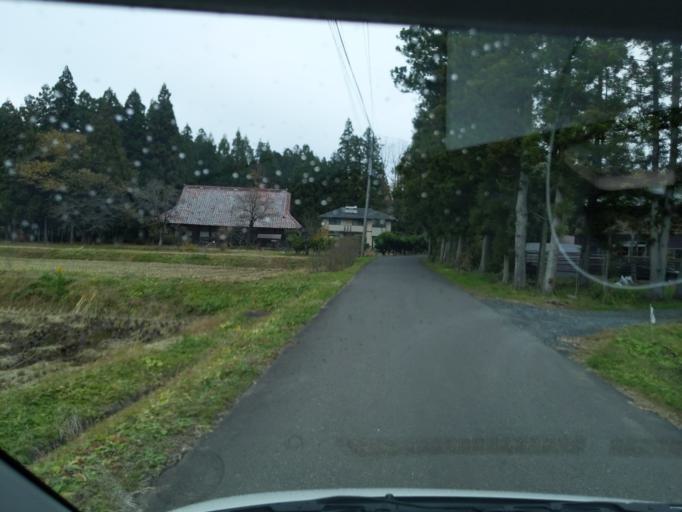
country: JP
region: Iwate
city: Ichinoseki
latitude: 38.9719
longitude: 140.9976
